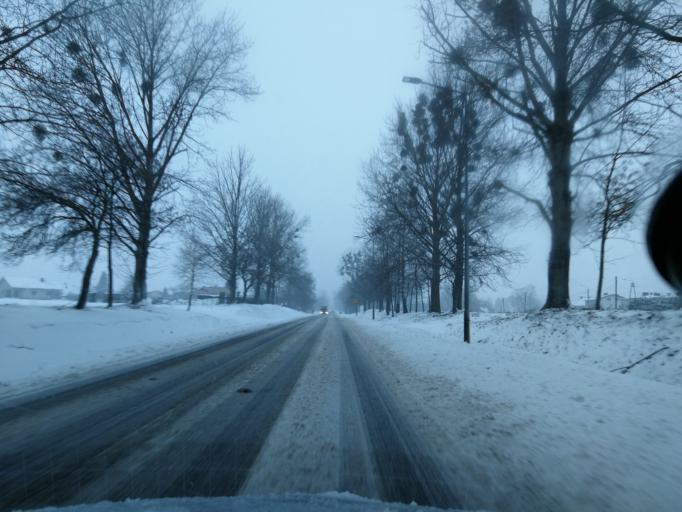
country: PL
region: Silesian Voivodeship
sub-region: Powiat pszczynski
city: Pszczyna
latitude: 49.9876
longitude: 18.9213
